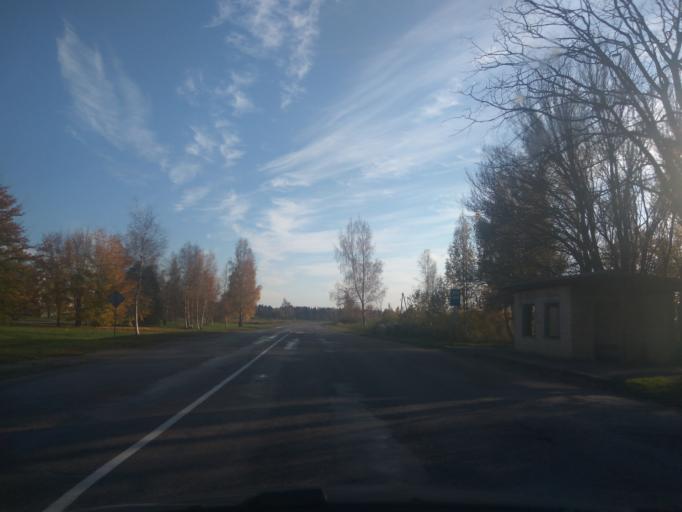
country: LV
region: Ventspils
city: Ventspils
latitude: 57.3047
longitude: 21.5591
